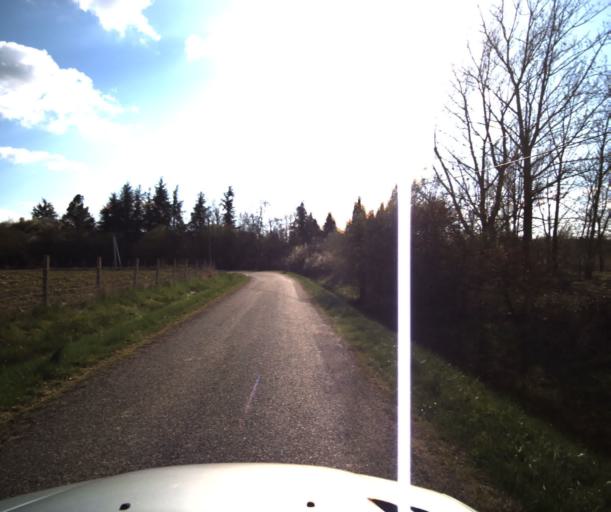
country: FR
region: Midi-Pyrenees
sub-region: Departement du Tarn-et-Garonne
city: Bressols
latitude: 43.9594
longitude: 1.2862
